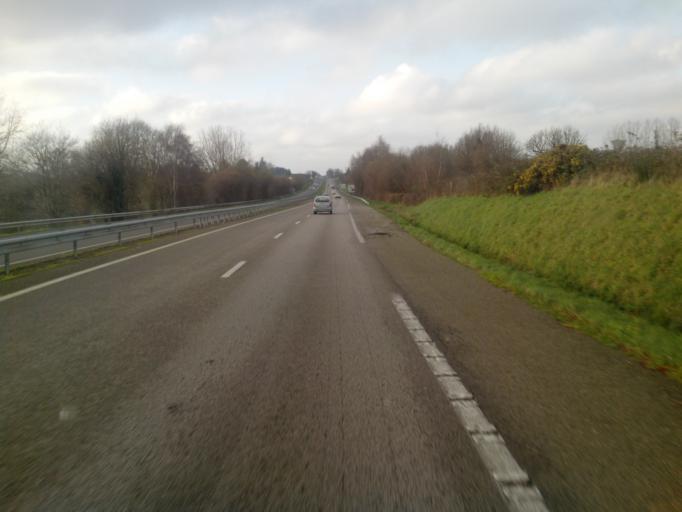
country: FR
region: Brittany
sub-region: Departement du Morbihan
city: Josselin
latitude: 47.9465
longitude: -2.5155
